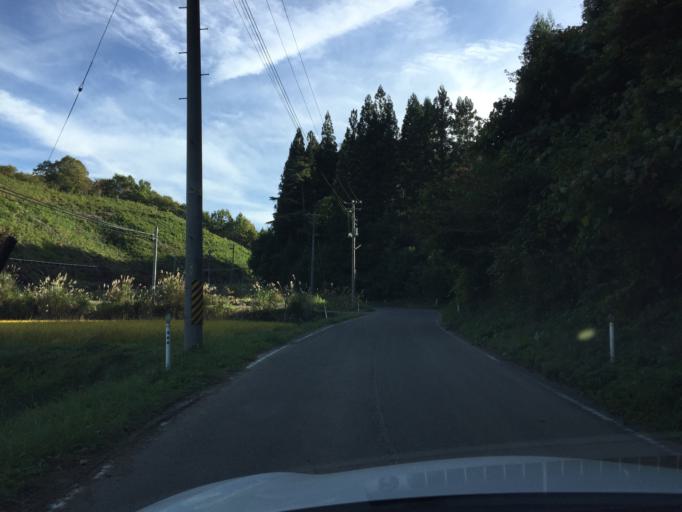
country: JP
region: Fukushima
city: Ishikawa
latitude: 37.2534
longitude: 140.6075
